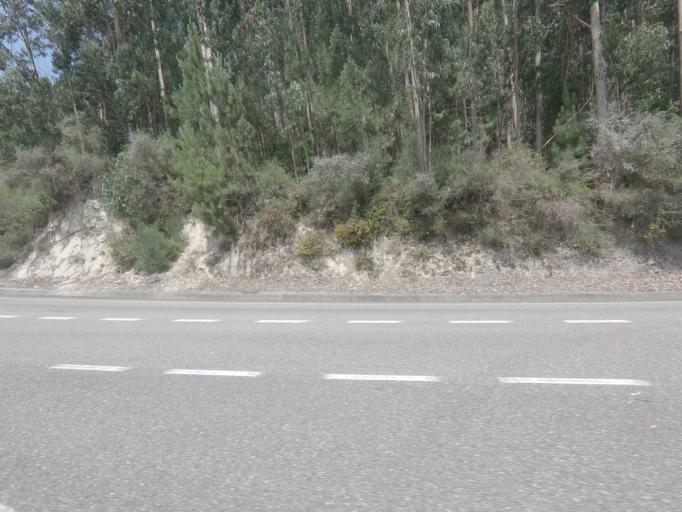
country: ES
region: Galicia
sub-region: Provincia de Pontevedra
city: Tomino
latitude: 42.0475
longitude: -8.7319
